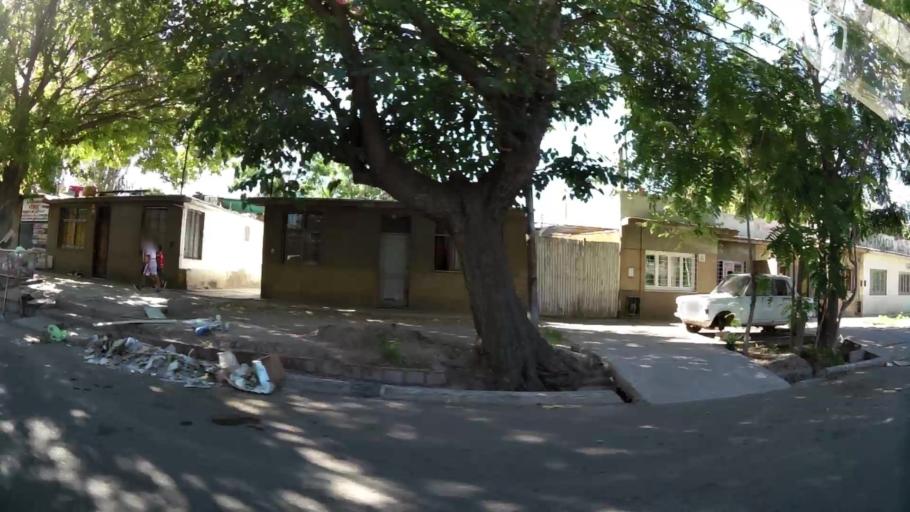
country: AR
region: Mendoza
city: Las Heras
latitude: -32.8420
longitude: -68.8245
